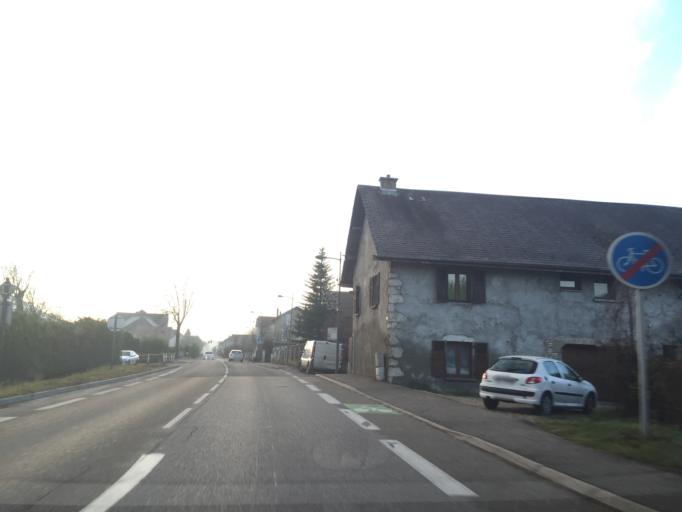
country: FR
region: Rhone-Alpes
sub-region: Departement de la Savoie
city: Viviers-du-Lac
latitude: 45.6527
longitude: 5.9082
